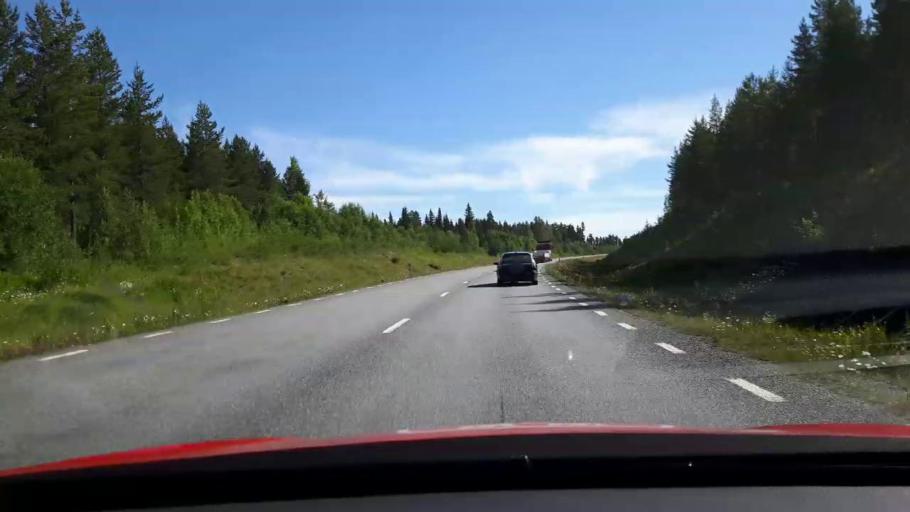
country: SE
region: Jaemtland
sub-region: OEstersunds Kommun
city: Lit
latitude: 63.3874
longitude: 14.8972
